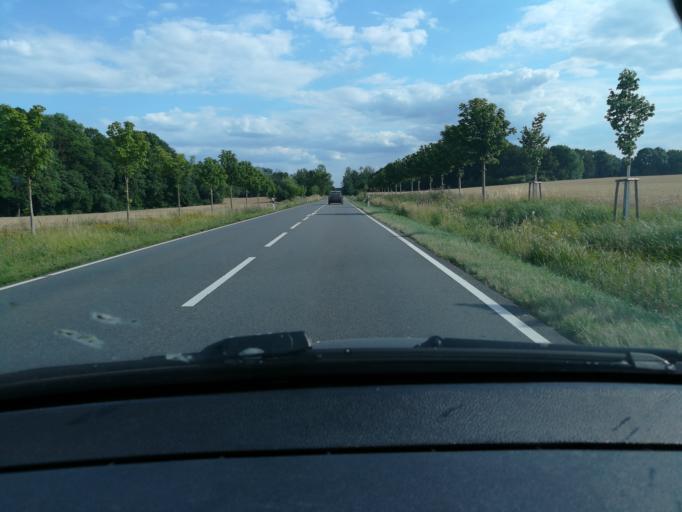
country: DE
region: Mecklenburg-Vorpommern
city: Klink
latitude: 53.4374
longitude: 12.5576
